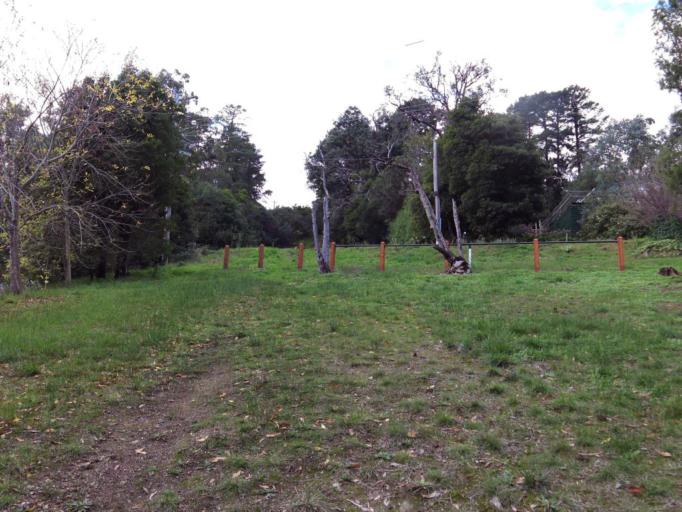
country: AU
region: Victoria
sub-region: Yarra Ranges
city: Mount Evelyn
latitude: -37.7850
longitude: 145.3638
